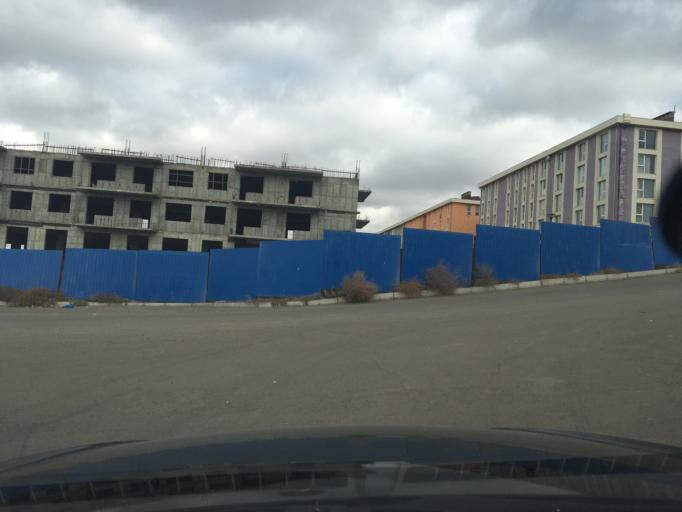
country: MN
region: Ulaanbaatar
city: Ulaanbaatar
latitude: 47.8802
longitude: 106.8489
